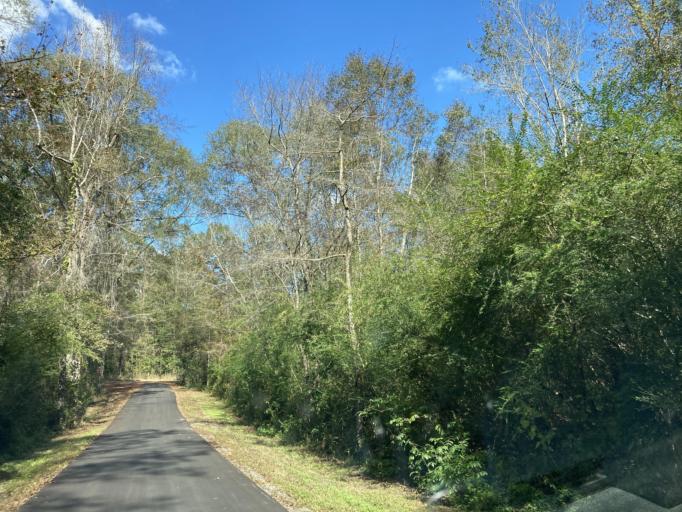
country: US
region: Mississippi
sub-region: Lamar County
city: Purvis
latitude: 31.2361
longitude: -89.4295
